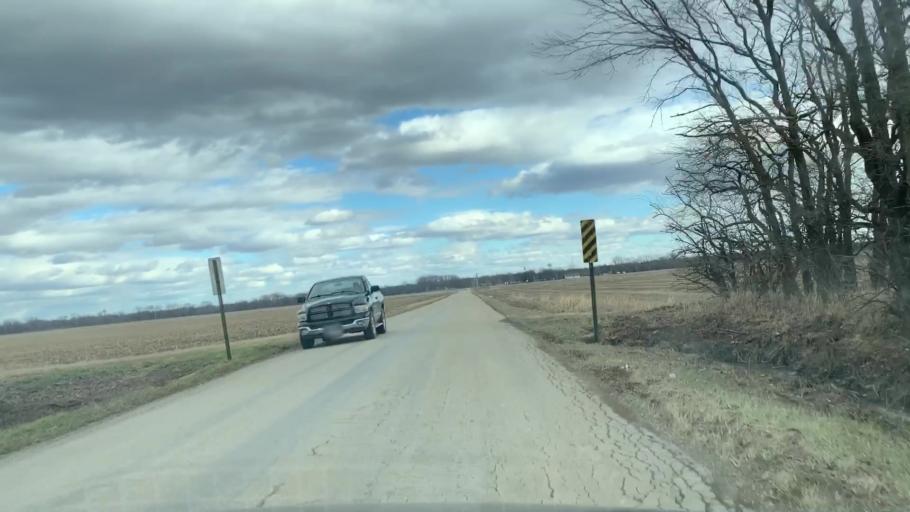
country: US
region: Kansas
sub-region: Allen County
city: Humboldt
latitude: 37.8129
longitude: -95.4666
